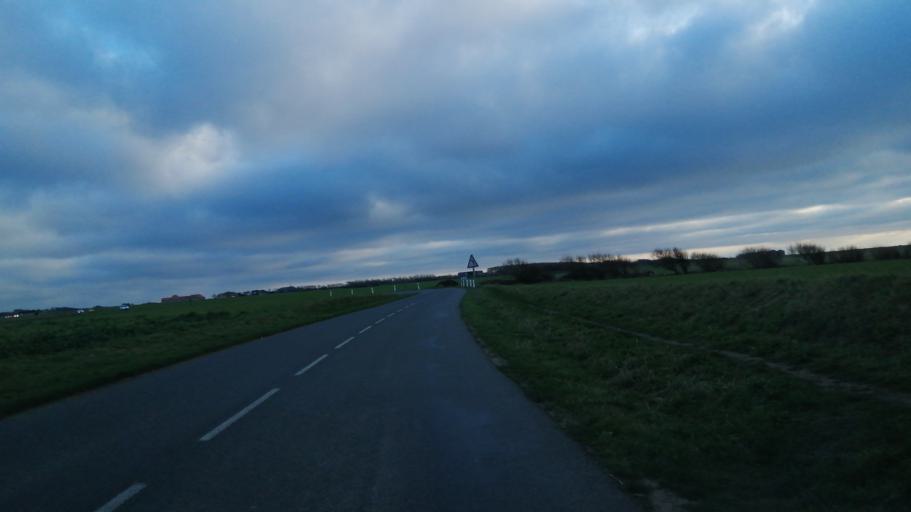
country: FR
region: Nord-Pas-de-Calais
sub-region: Departement du Pas-de-Calais
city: Ambleteuse
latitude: 50.8528
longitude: 1.5949
